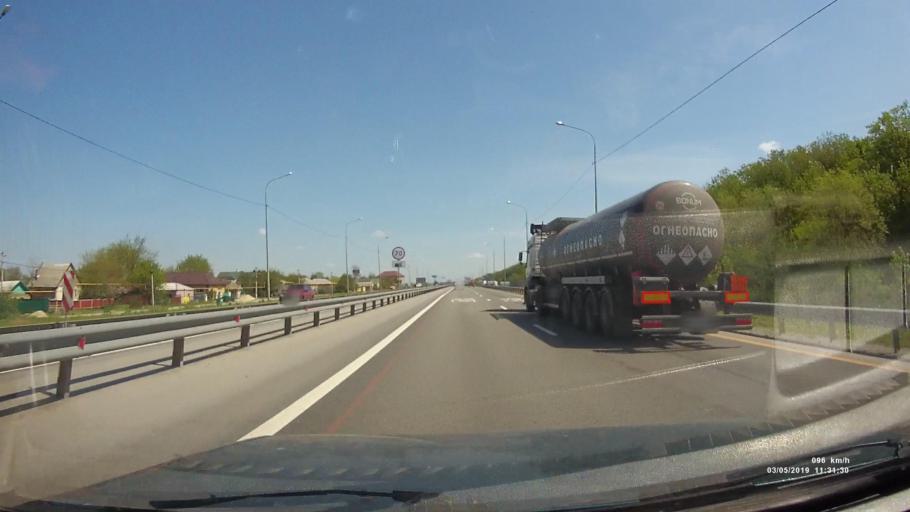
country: RU
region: Rostov
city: Bataysk
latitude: 47.1075
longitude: 39.8378
